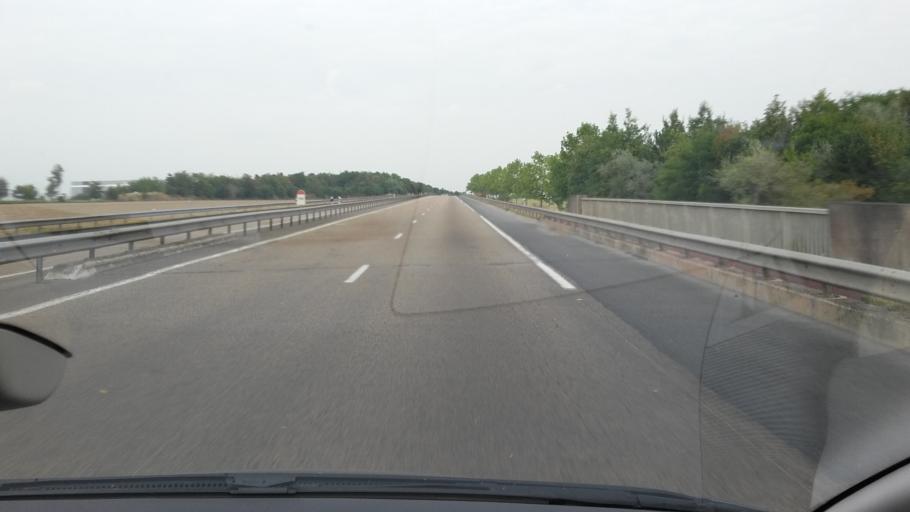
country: FR
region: Champagne-Ardenne
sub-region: Departement de la Marne
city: Witry-les-Reims
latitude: 49.2967
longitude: 4.1316
